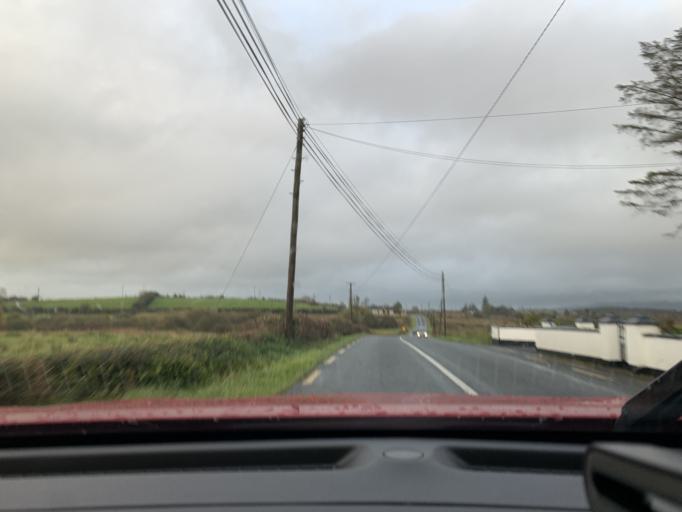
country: IE
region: Connaught
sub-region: Sligo
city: Ballymote
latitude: 54.0127
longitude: -8.5237
